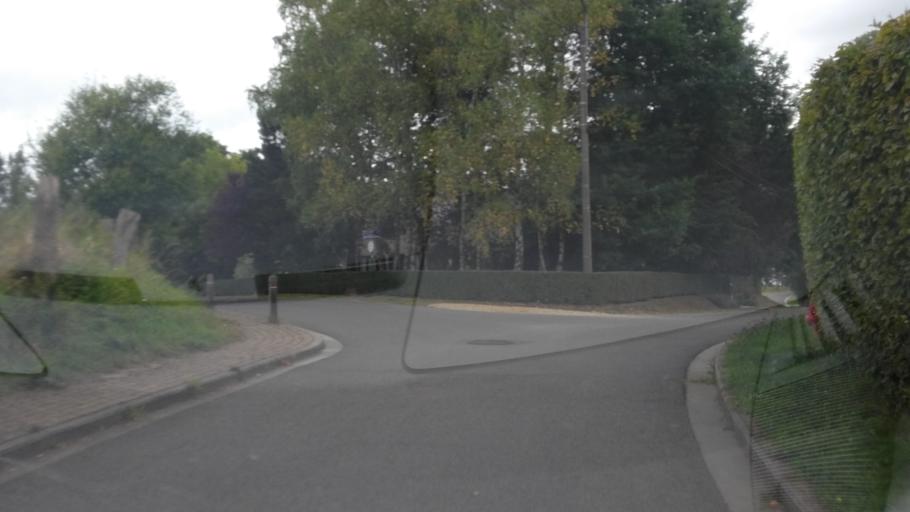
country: BE
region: Wallonia
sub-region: Province du Luxembourg
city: Arlon
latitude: 49.6859
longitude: 5.8417
